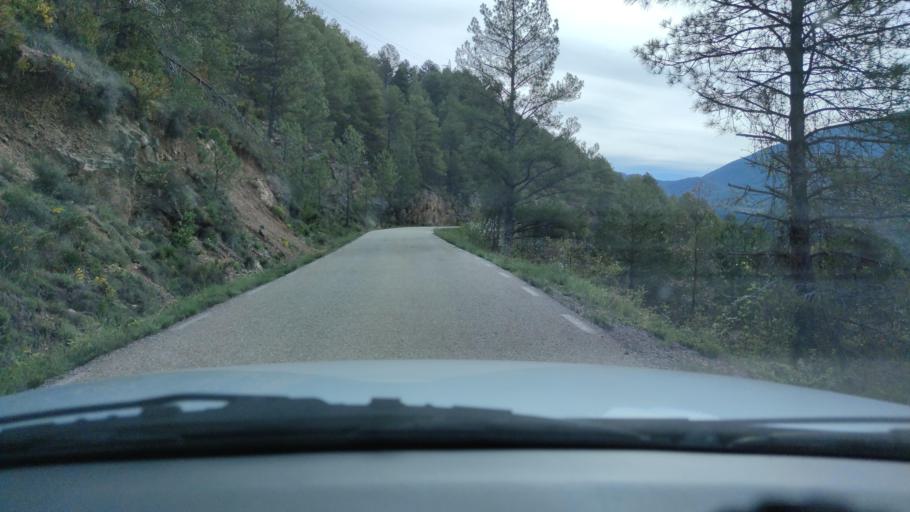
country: ES
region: Catalonia
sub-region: Provincia de Lleida
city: la Seu d'Urgell
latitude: 42.2341
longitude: 1.4695
